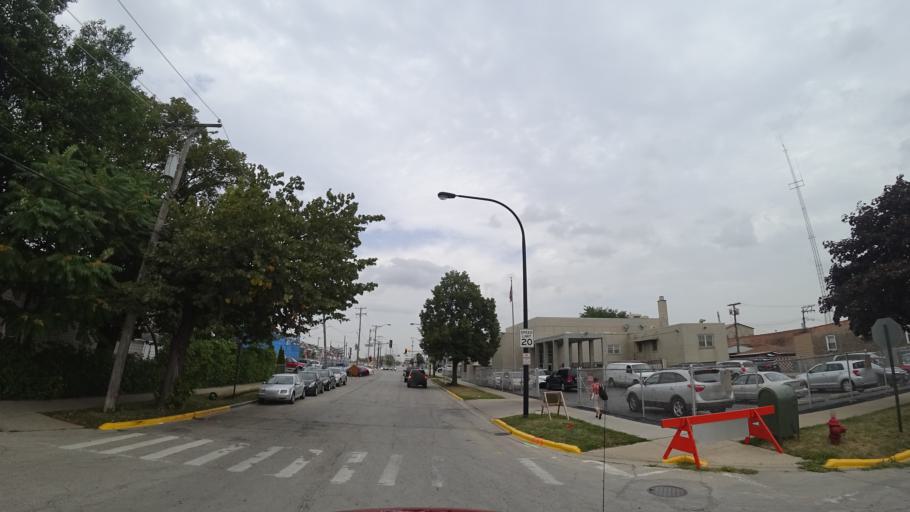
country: US
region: Illinois
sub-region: Cook County
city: Cicero
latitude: 41.8501
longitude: -87.7590
